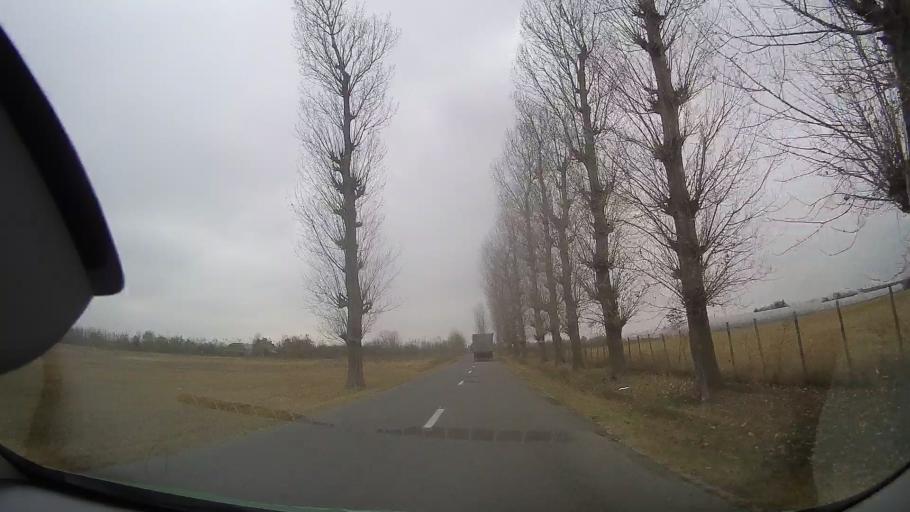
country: RO
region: Ialomita
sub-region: Comuna Valea Macrisului
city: Valea Macrisului
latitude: 44.7388
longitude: 26.8429
